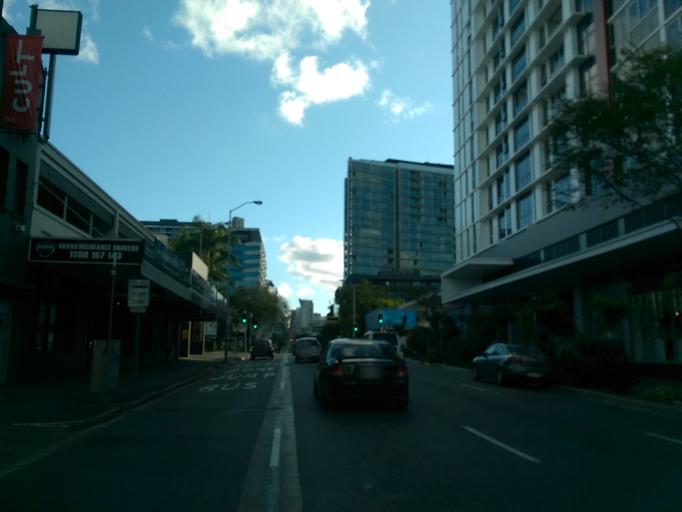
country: AU
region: Queensland
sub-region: Brisbane
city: Fortitude Valley
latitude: -27.4539
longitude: 153.0396
